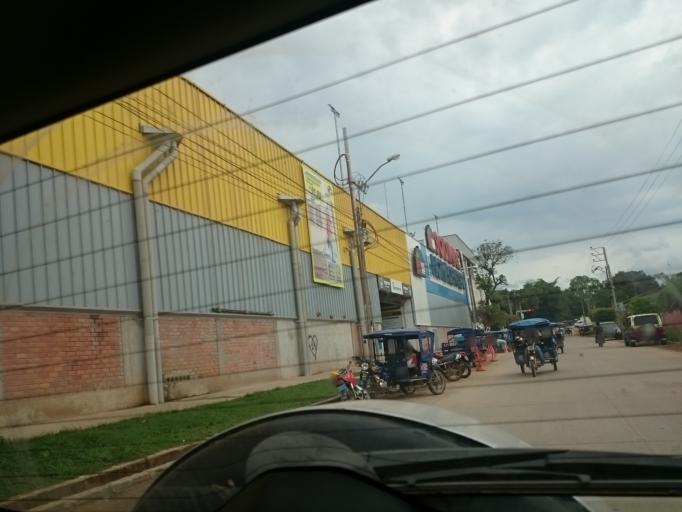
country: PE
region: Ucayali
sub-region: Provincia de Coronel Portillo
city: Pucallpa
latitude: -8.3872
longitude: -74.5674
